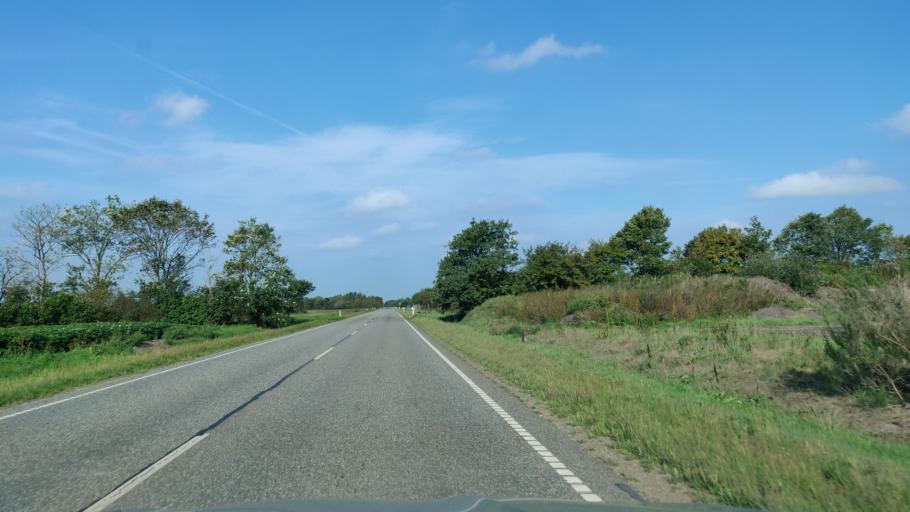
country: DK
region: Central Jutland
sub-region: Herning Kommune
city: Sunds
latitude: 56.2517
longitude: 9.0550
